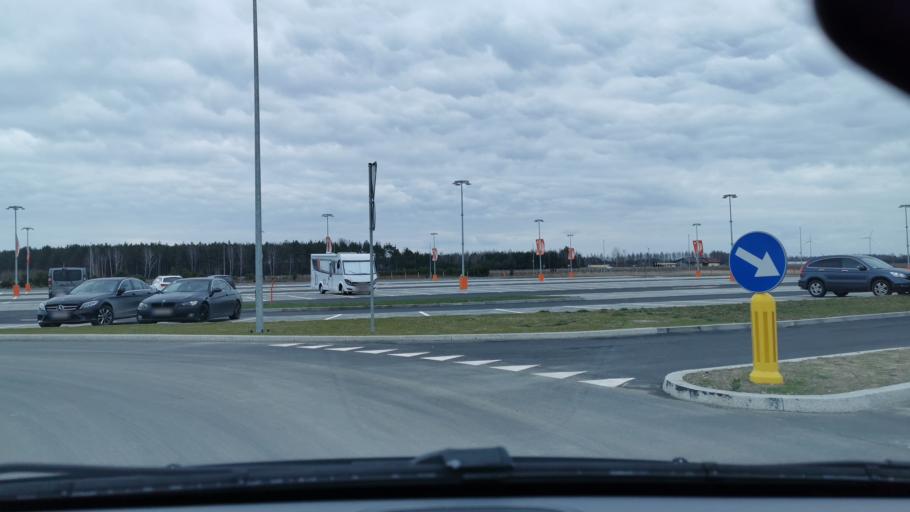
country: PL
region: Masovian Voivodeship
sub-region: Powiat zyrardowski
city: Mszczonow
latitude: 51.9875
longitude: 20.4617
